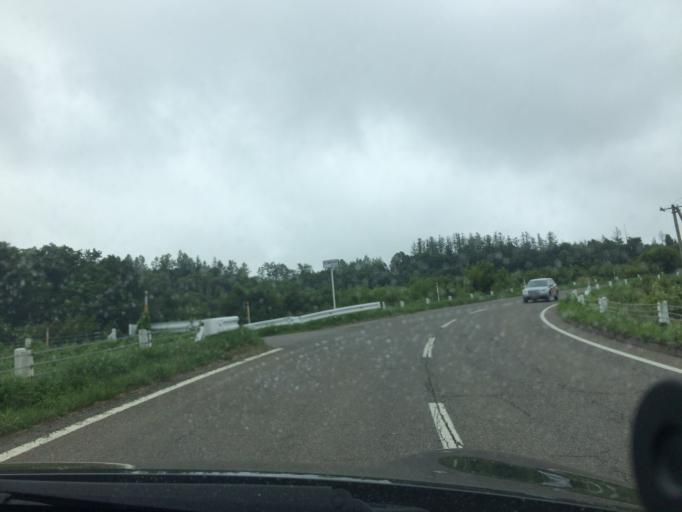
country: JP
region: Hokkaido
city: Otofuke
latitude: 42.9577
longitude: 143.0778
